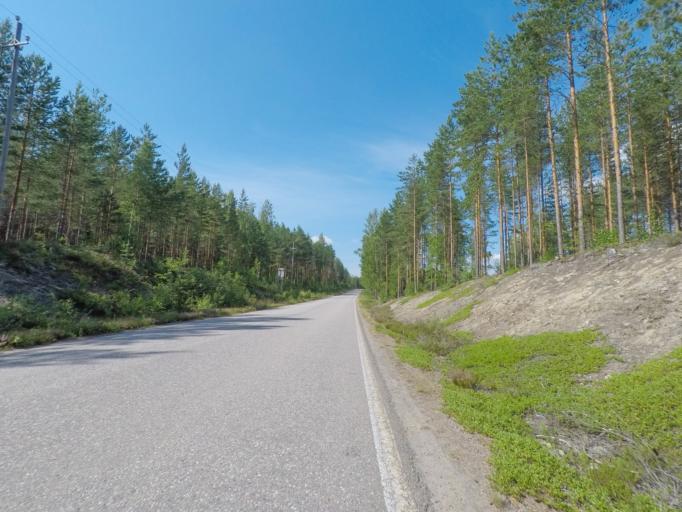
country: FI
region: Southern Savonia
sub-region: Mikkeli
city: Puumala
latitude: 61.4628
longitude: 28.1733
